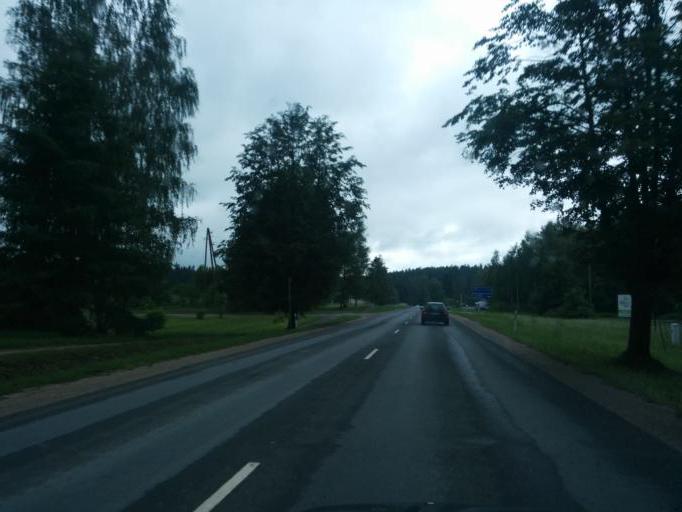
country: LV
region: Smiltene
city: Smiltene
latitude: 57.4142
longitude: 25.9335
